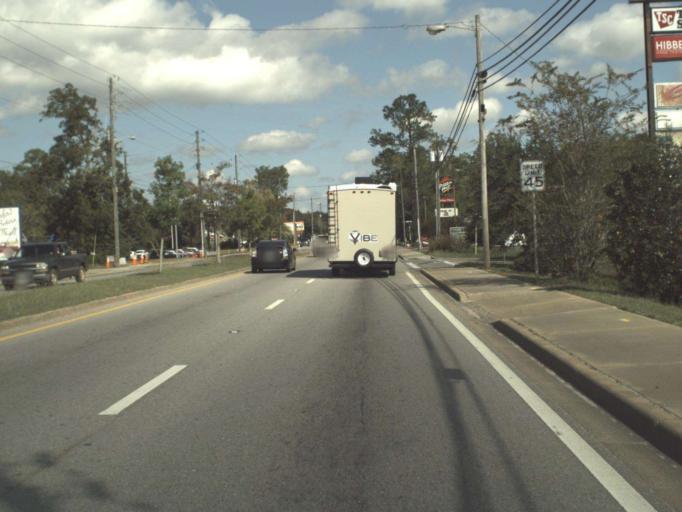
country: US
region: Florida
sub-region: Walton County
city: DeFuniak Springs
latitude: 30.7082
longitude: -86.1227
